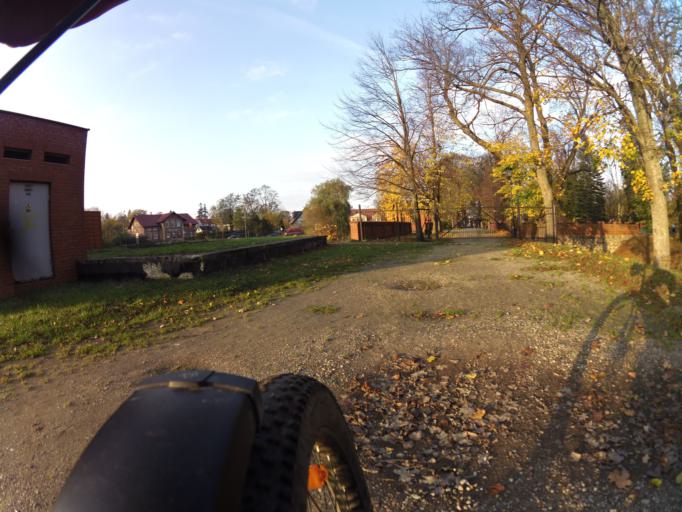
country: PL
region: Pomeranian Voivodeship
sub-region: Powiat pucki
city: Krokowa
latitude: 54.7767
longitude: 18.1626
